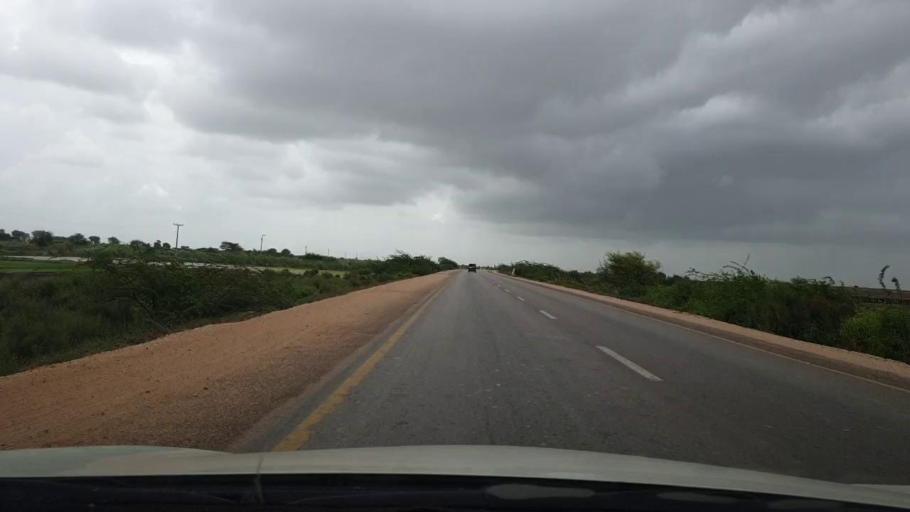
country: PK
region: Sindh
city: Mirpur Batoro
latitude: 24.6437
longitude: 68.4343
